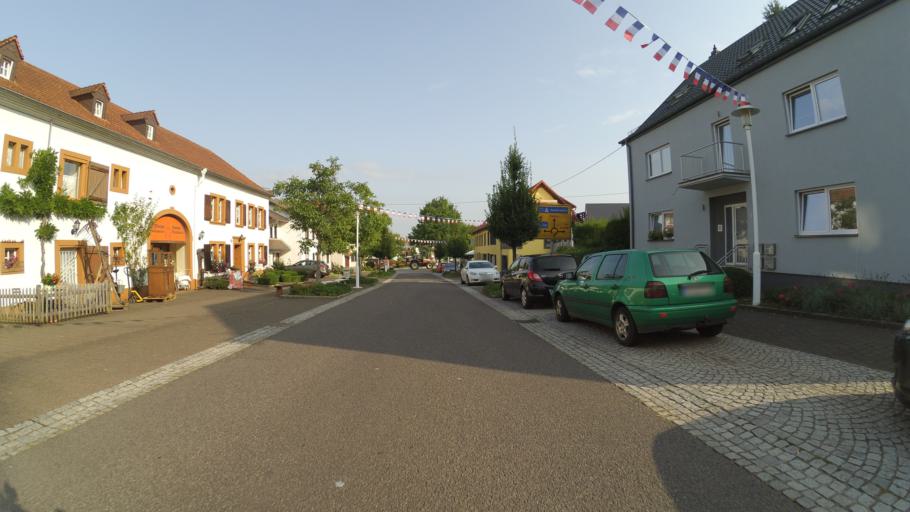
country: DE
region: Saarland
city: Weiskirchen
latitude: 49.5552
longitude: 6.8224
